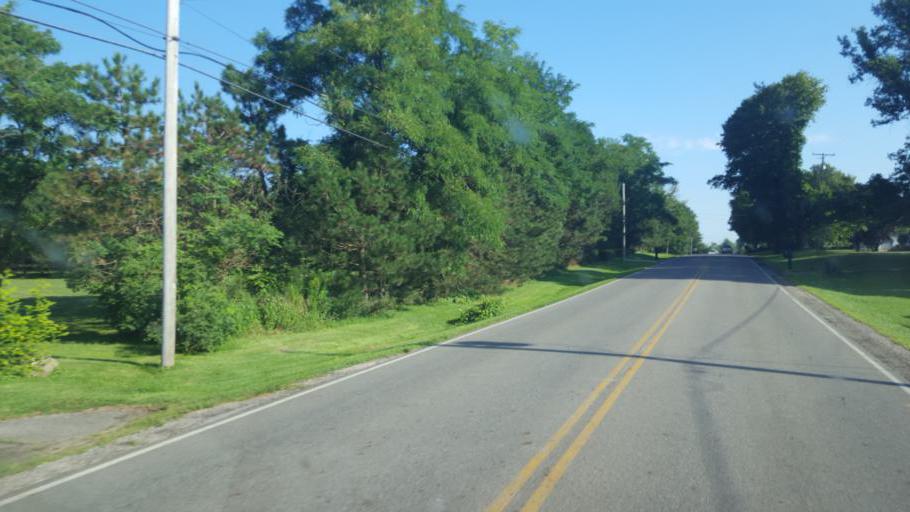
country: US
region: Ohio
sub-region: Richland County
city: Ontario
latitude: 40.7371
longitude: -82.5895
